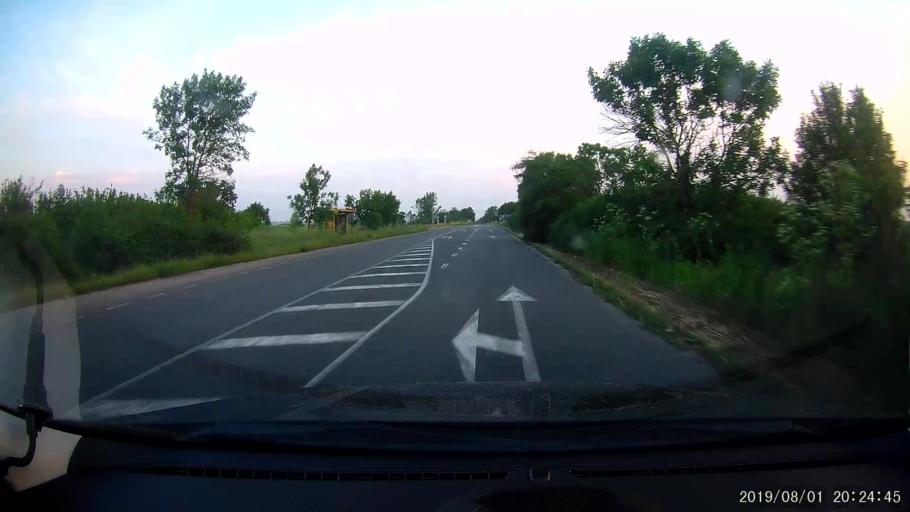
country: BG
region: Yambol
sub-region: Obshtina Elkhovo
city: Elkhovo
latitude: 42.2267
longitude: 26.5916
